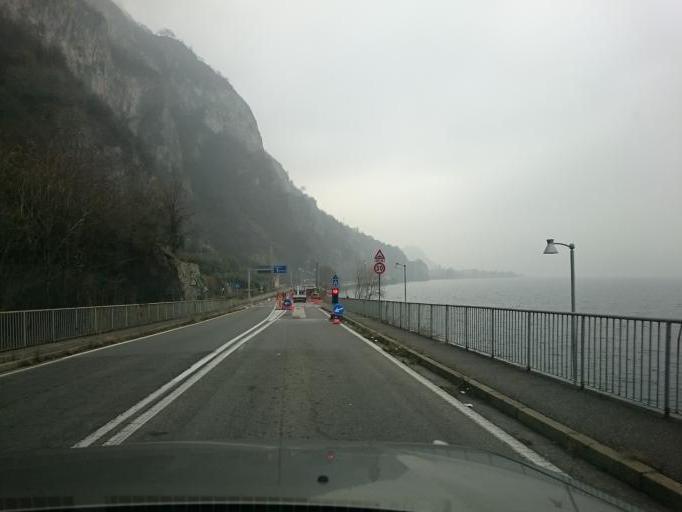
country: IT
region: Lombardy
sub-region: Provincia di Brescia
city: Marone
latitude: 45.7506
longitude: 10.0858
